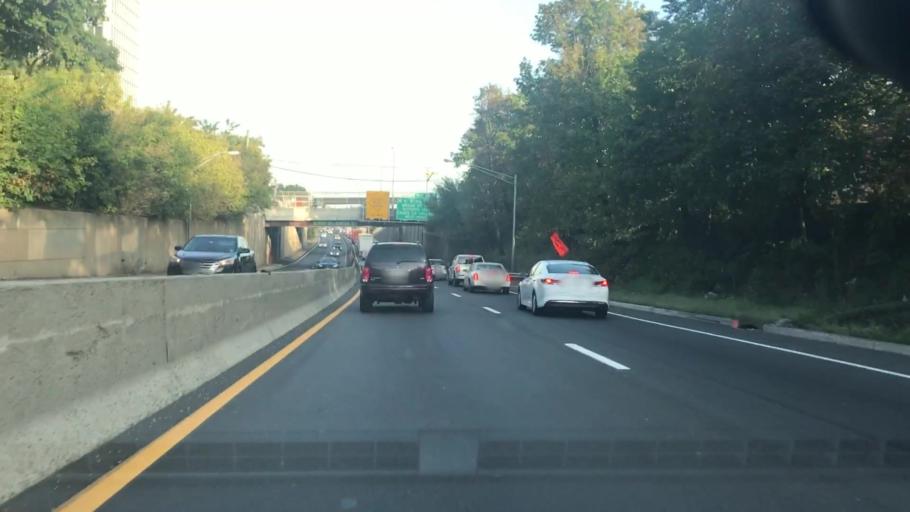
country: US
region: New Jersey
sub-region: Essex County
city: Newark
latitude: 40.7502
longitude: -74.1818
